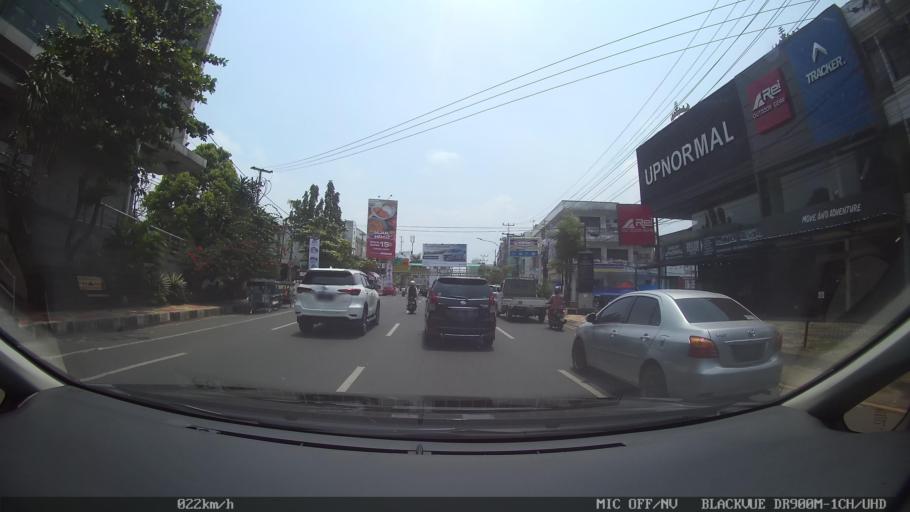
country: ID
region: Lampung
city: Bandarlampung
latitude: -5.4201
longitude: 105.2526
